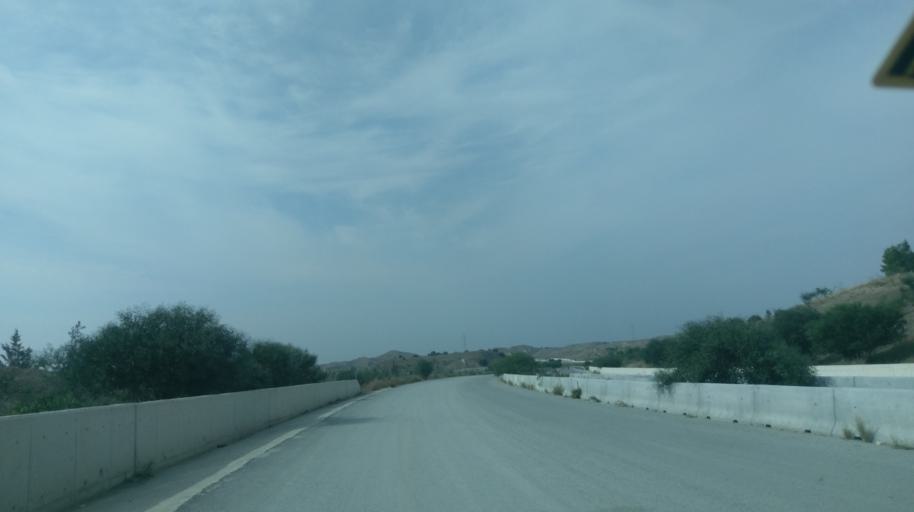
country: CY
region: Lefkosia
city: Nicosia
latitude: 35.2300
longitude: 33.4049
